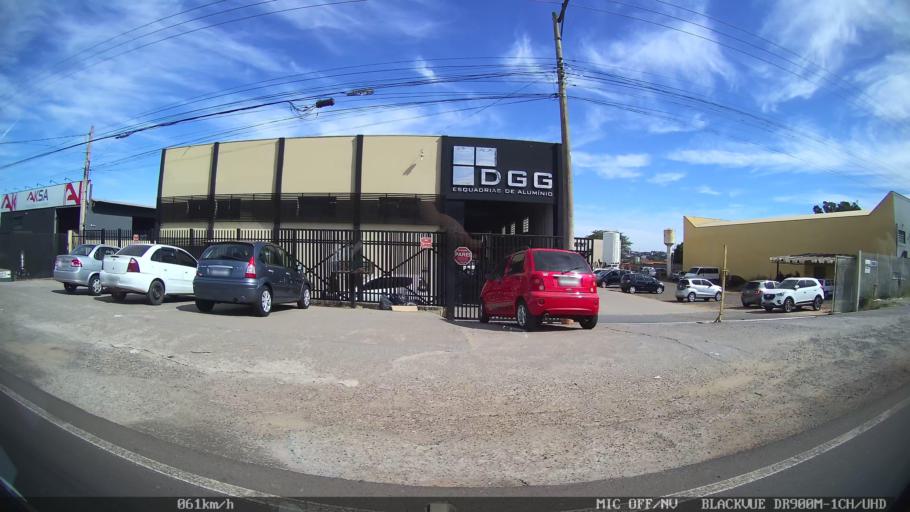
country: BR
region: Sao Paulo
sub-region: Sao Jose Do Rio Preto
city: Sao Jose do Rio Preto
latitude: -20.8343
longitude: -49.3381
